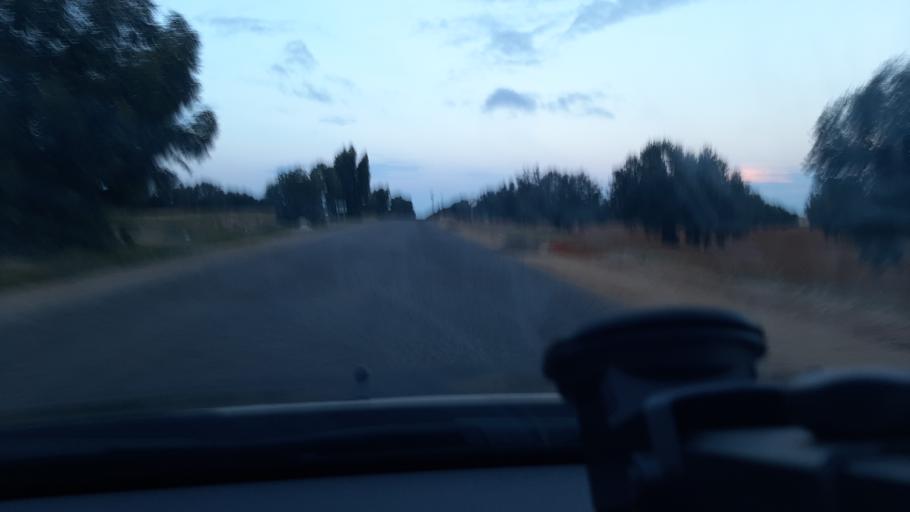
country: TN
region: Al Mahdiyah
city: Shurban
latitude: 34.9736
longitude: 10.3758
